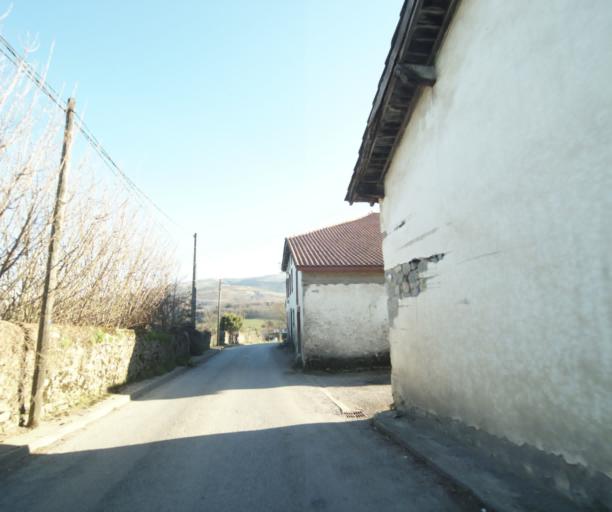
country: FR
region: Aquitaine
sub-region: Departement des Pyrenees-Atlantiques
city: Urrugne
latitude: 43.3573
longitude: -1.7255
